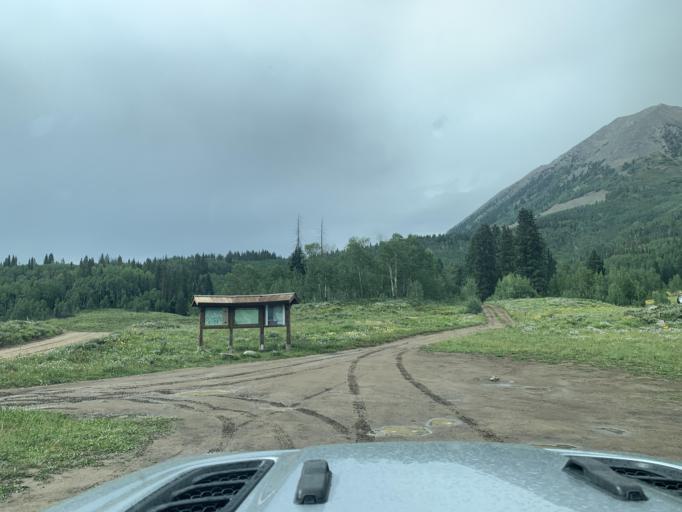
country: US
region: Colorado
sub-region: Gunnison County
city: Crested Butte
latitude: 38.9332
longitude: -107.0137
